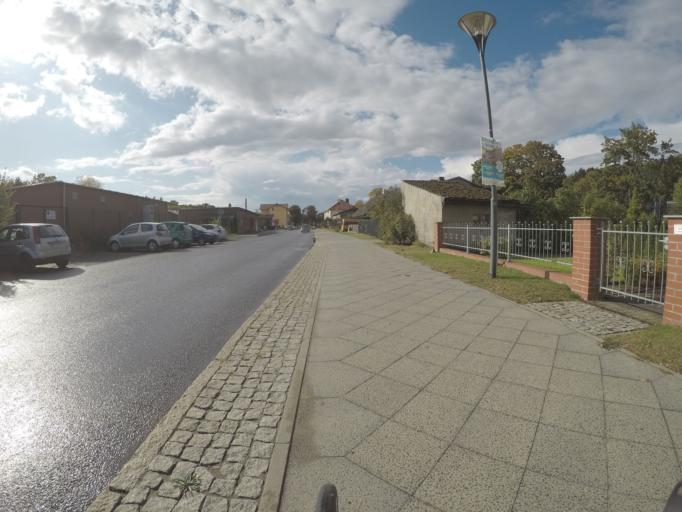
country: DE
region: Brandenburg
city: Petershagen
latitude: 52.5322
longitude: 13.8378
